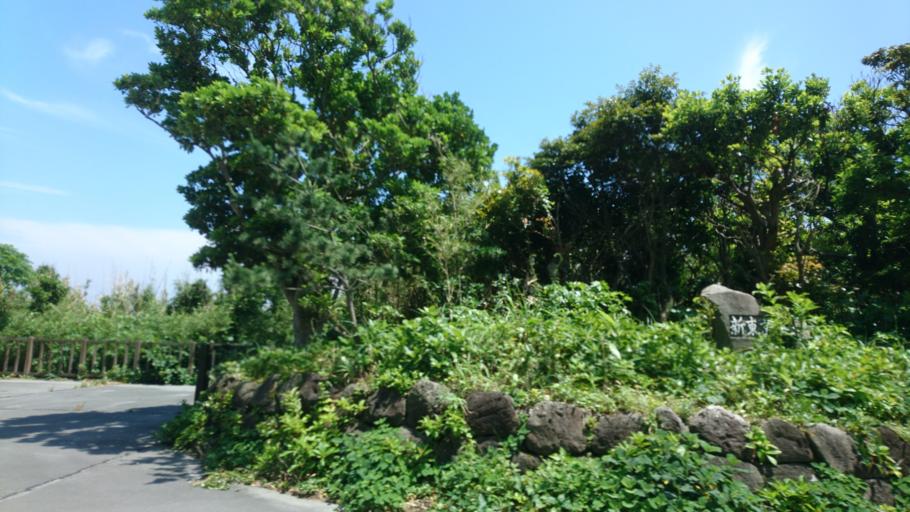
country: JP
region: Shizuoka
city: Shimoda
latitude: 34.3926
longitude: 139.2782
